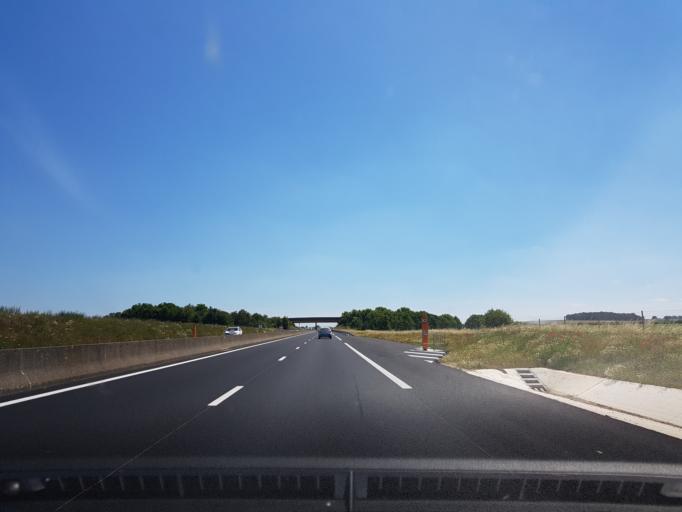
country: FR
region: Picardie
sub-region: Departement de la Somme
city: Nesle
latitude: 49.8355
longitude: 2.9419
